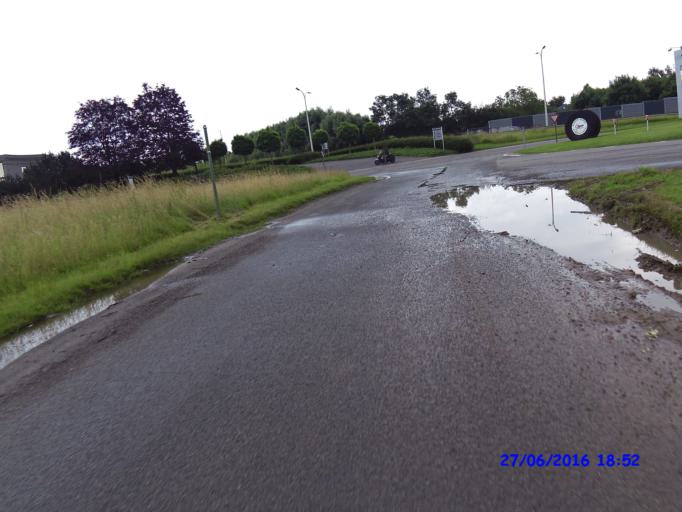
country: BE
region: Flanders
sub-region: Provincie Vlaams-Brabant
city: Wemmel
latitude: 50.8915
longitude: 4.2692
